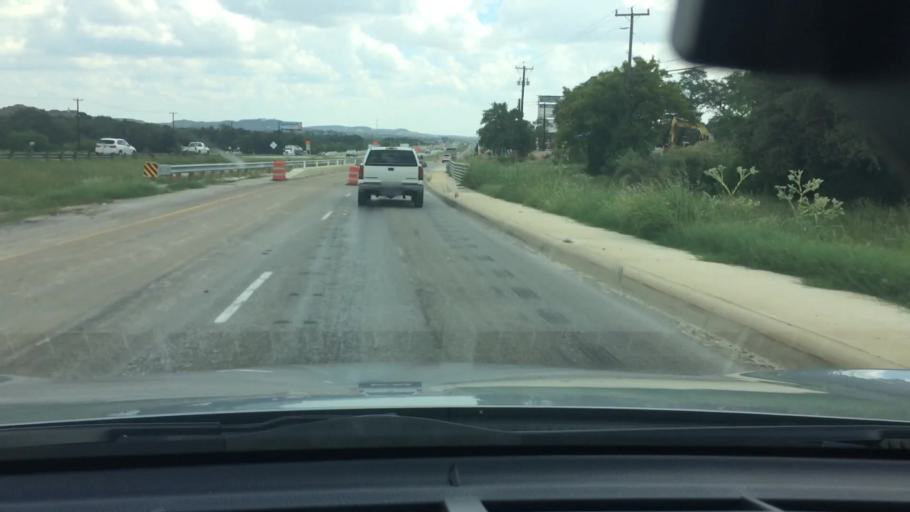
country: US
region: Texas
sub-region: Bexar County
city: Scenic Oaks
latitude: 29.7098
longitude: -98.6594
